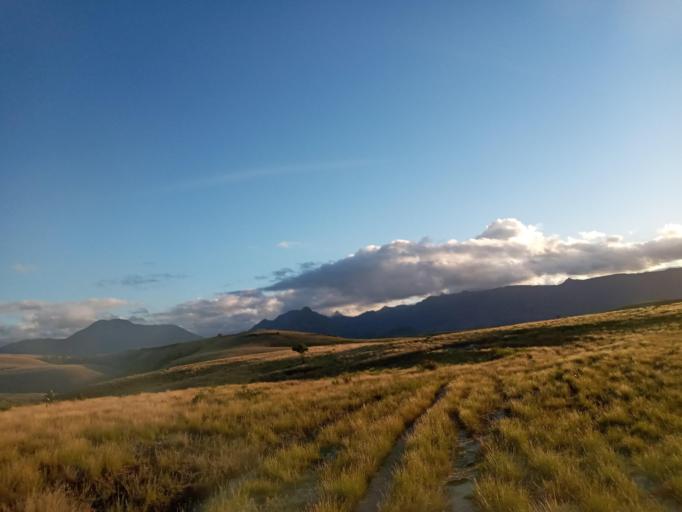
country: MG
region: Anosy
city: Fort Dauphin
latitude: -24.5117
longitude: 47.2562
